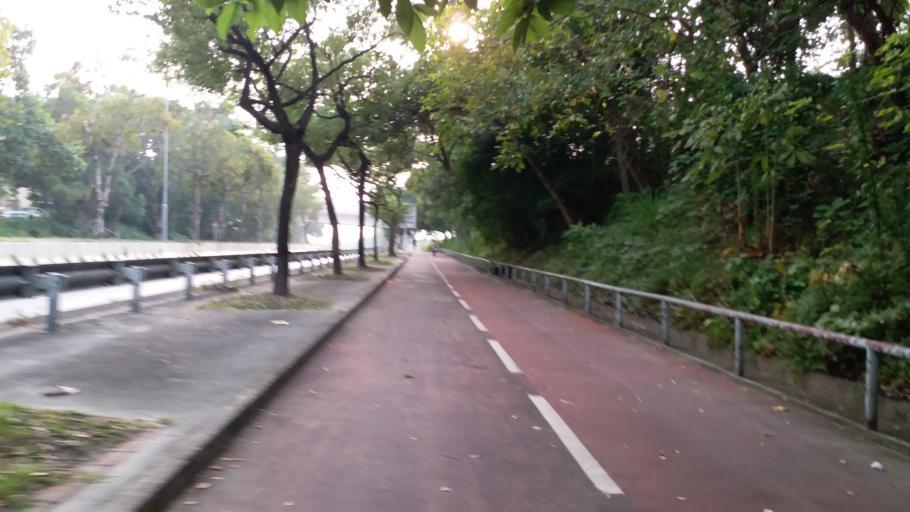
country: HK
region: Yuen Long
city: Yuen Long Kau Hui
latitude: 22.4493
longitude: 114.0204
